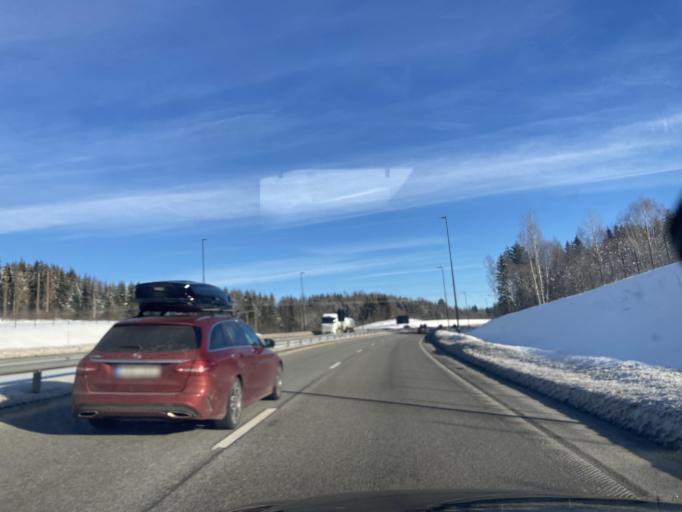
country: NO
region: Hedmark
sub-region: Loten
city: Loten
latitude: 60.8343
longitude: 11.2951
